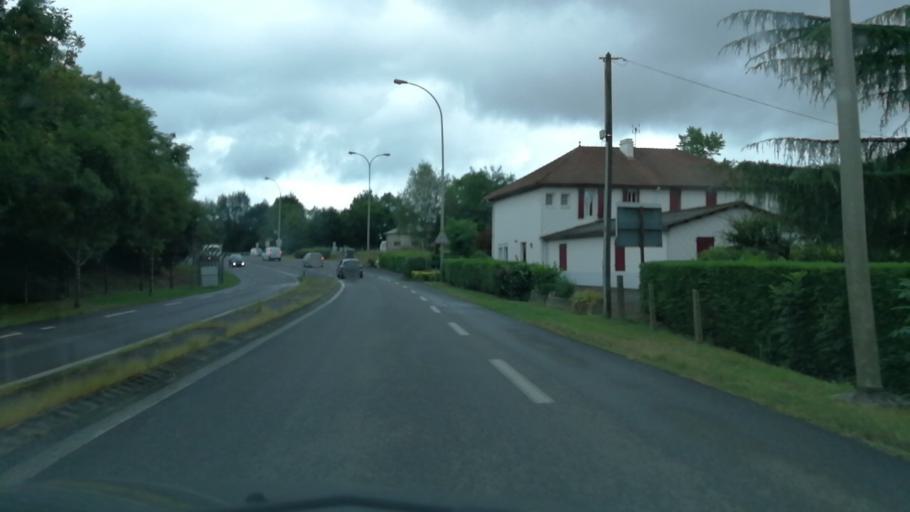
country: FR
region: Aquitaine
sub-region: Departement des Pyrenees-Atlantiques
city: Mourenx
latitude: 43.3852
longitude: -0.5890
